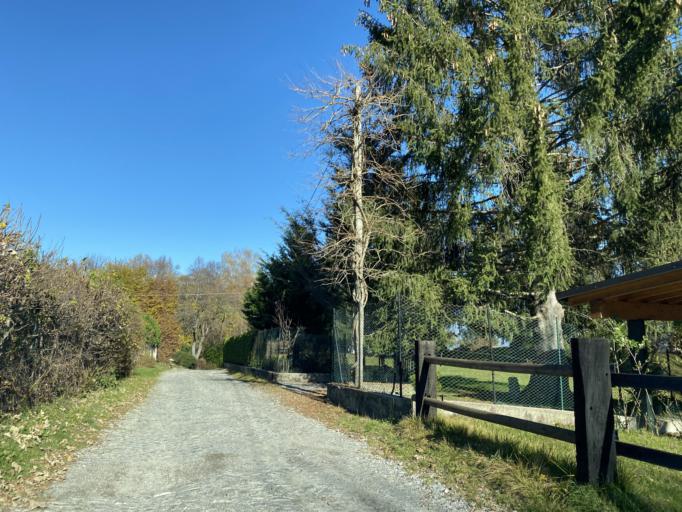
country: IT
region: Lombardy
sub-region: Provincia di Como
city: Pellio Intelvi
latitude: 45.9732
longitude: 9.0501
